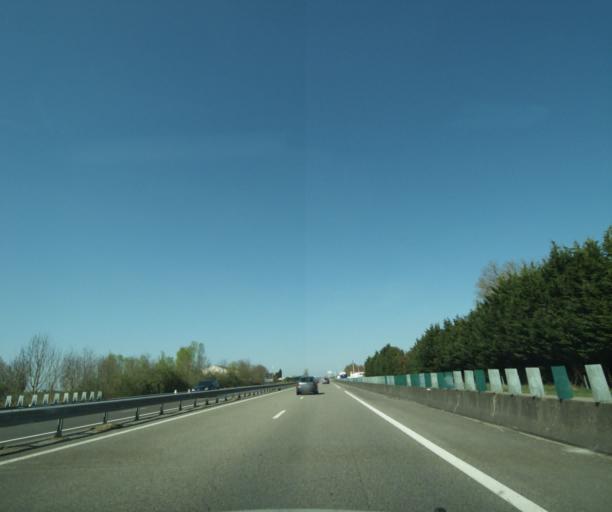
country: FR
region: Bourgogne
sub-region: Departement de la Nievre
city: Cosne-Cours-sur-Loire
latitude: 47.3769
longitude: 2.9232
